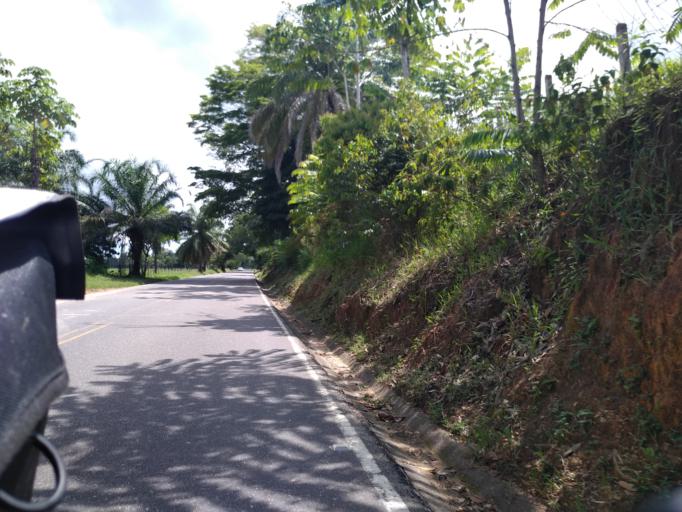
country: CO
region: Santander
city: Cimitarra
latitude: 6.4456
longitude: -74.0224
